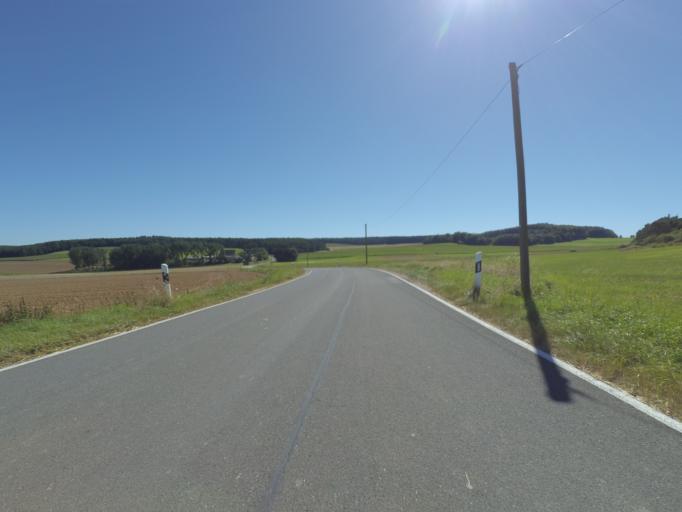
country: DE
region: Rheinland-Pfalz
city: Uxheim
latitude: 50.3319
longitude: 6.7536
